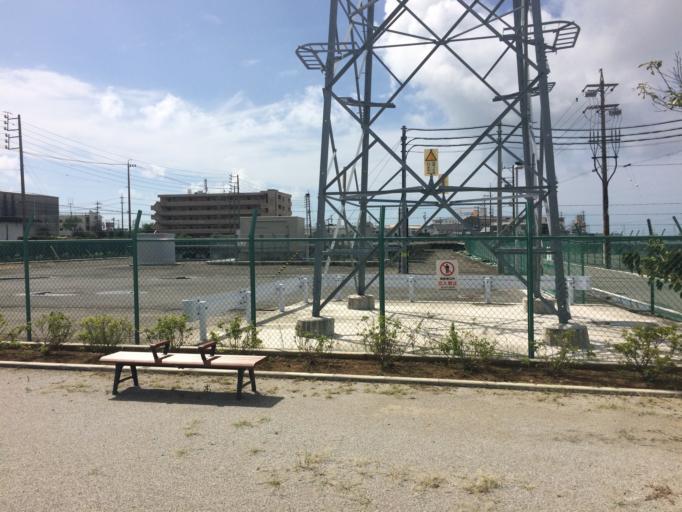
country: JP
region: Shizuoka
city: Shizuoka-shi
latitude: 35.0014
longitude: 138.5110
